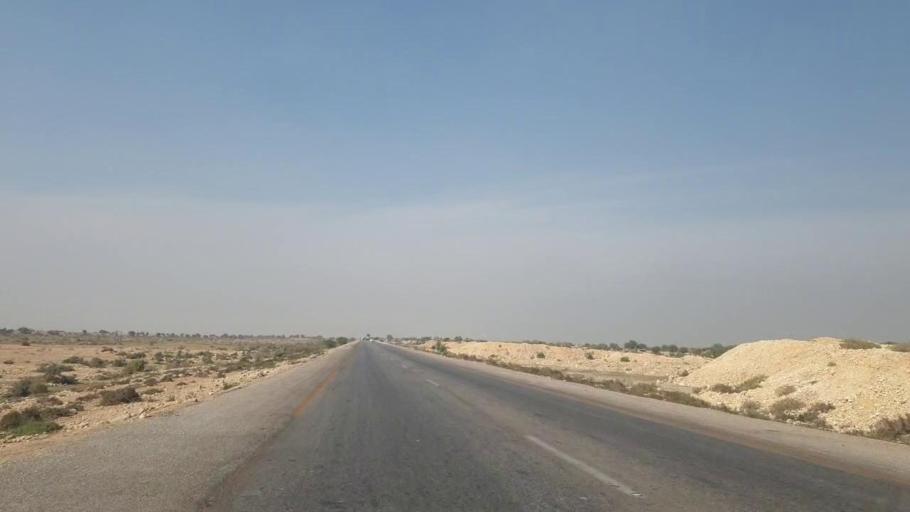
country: PK
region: Sindh
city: Hala
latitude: 25.8670
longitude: 68.2583
